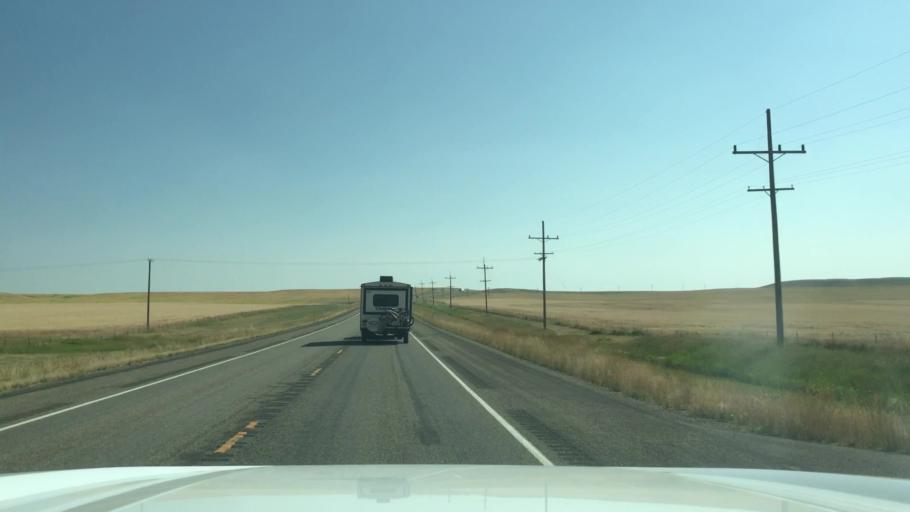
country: US
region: Montana
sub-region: Wheatland County
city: Harlowton
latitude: 46.4805
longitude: -109.7661
